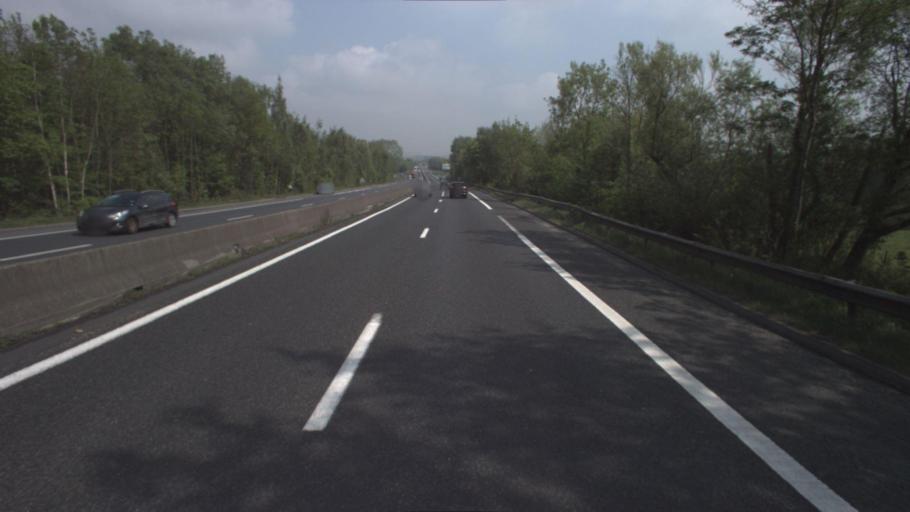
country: FR
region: Ile-de-France
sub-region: Departement de Seine-et-Marne
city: Saint-Mard
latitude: 49.0519
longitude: 2.6978
